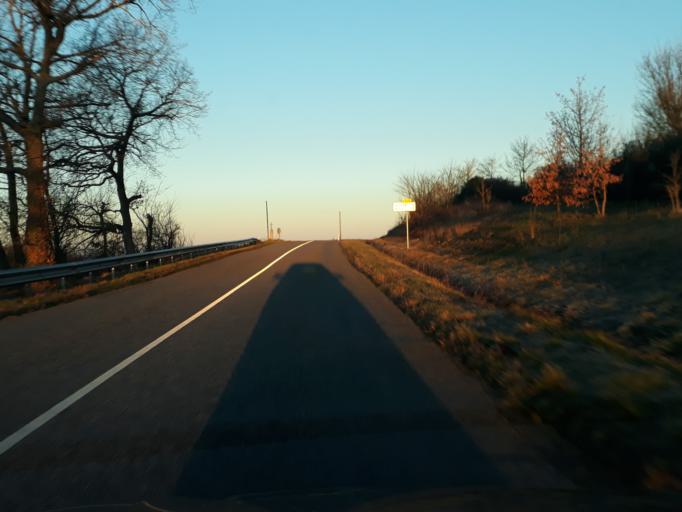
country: FR
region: Midi-Pyrenees
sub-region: Departement du Gers
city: Aubiet
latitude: 43.6012
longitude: 0.6968
